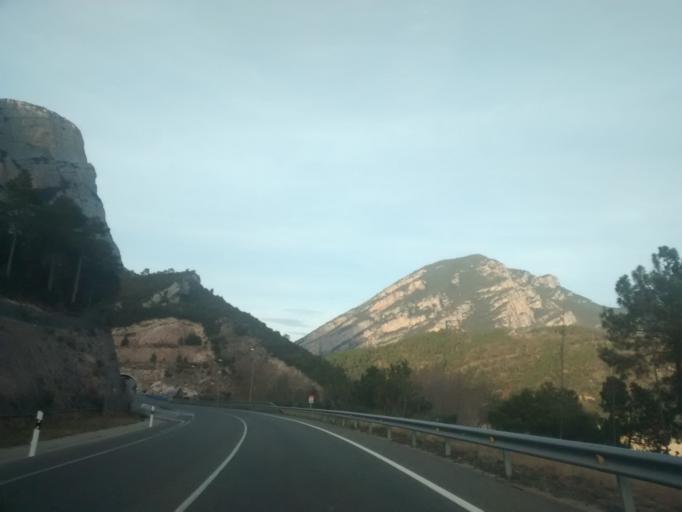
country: ES
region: Catalonia
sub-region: Provincia de Lleida
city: Oliana
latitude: 42.1155
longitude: 1.3034
